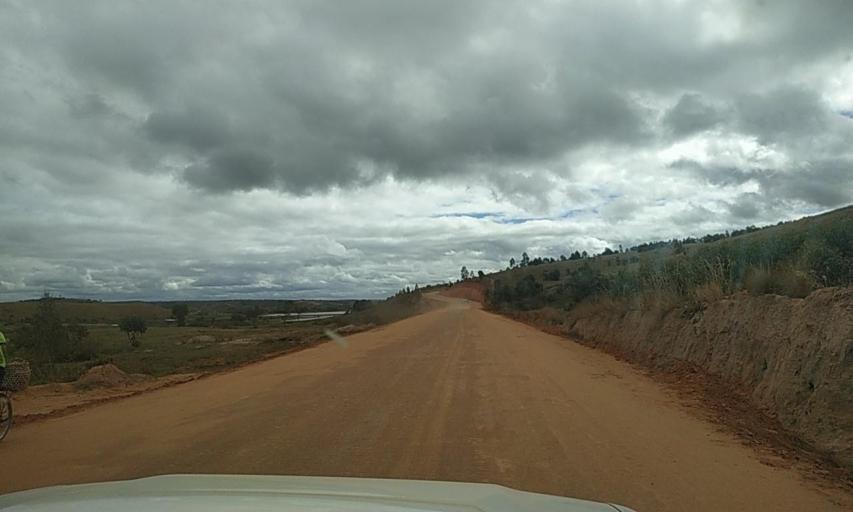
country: MG
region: Alaotra Mangoro
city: Ambatondrazaka
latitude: -17.9569
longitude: 48.2525
